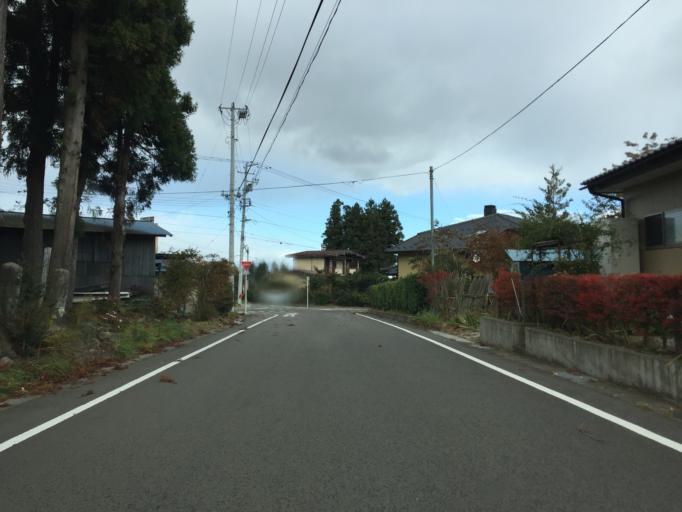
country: JP
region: Fukushima
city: Fukushima-shi
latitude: 37.7039
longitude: 140.3603
